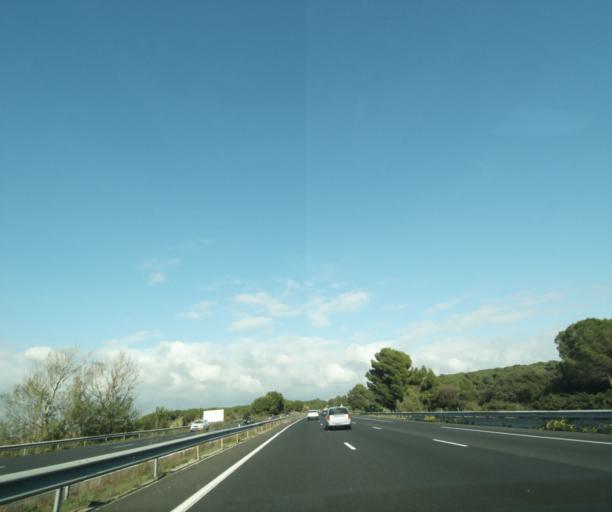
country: FR
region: Languedoc-Roussillon
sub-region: Departement de l'Aude
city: Vinassan
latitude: 43.2208
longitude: 3.0944
